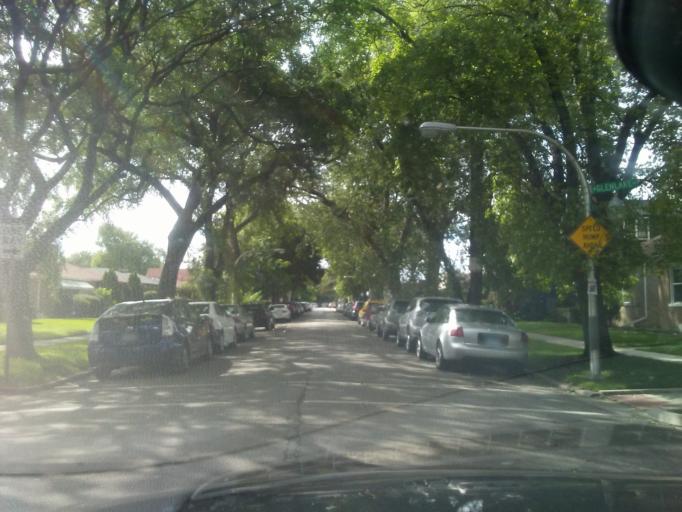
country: US
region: Illinois
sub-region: Cook County
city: Lincolnwood
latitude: 41.9922
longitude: -87.6922
